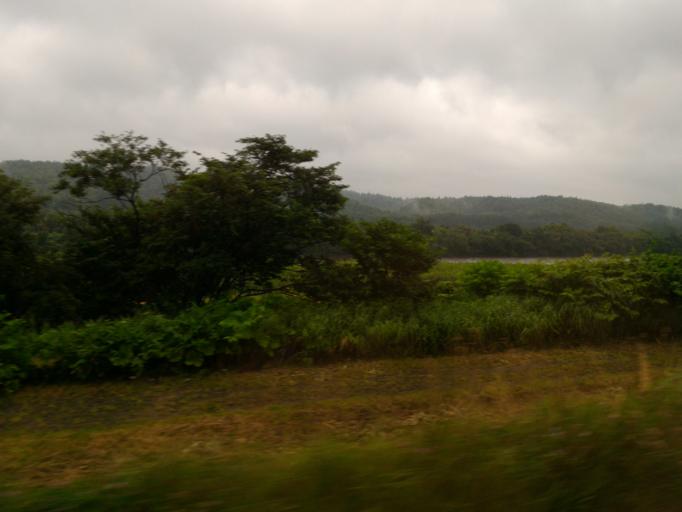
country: JP
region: Hokkaido
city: Nayoro
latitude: 44.7550
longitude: 142.0473
